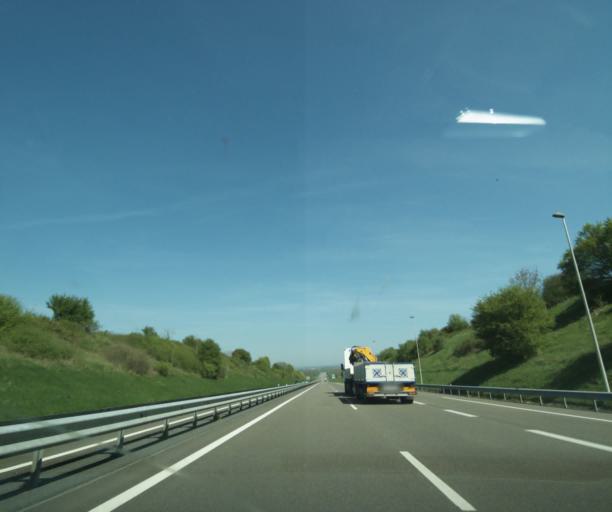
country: FR
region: Bourgogne
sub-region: Departement de la Nievre
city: Challuy
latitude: 46.9426
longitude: 3.1614
